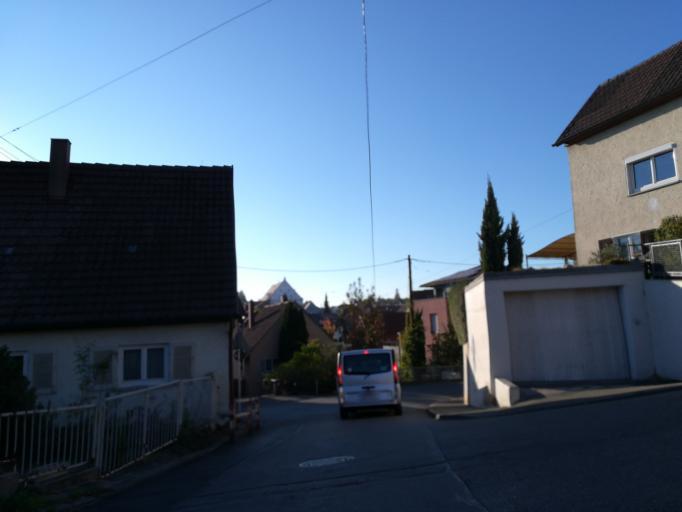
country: DE
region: Baden-Wuerttemberg
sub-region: Regierungsbezirk Stuttgart
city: Neuhausen auf den Fildern
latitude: 48.6834
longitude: 9.2819
